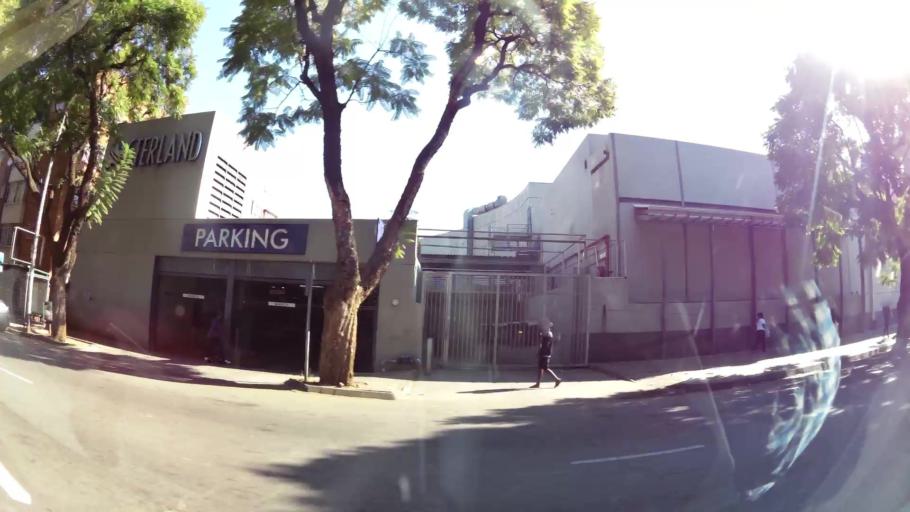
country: ZA
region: Gauteng
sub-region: City of Tshwane Metropolitan Municipality
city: Pretoria
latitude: -25.7476
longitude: 28.2040
